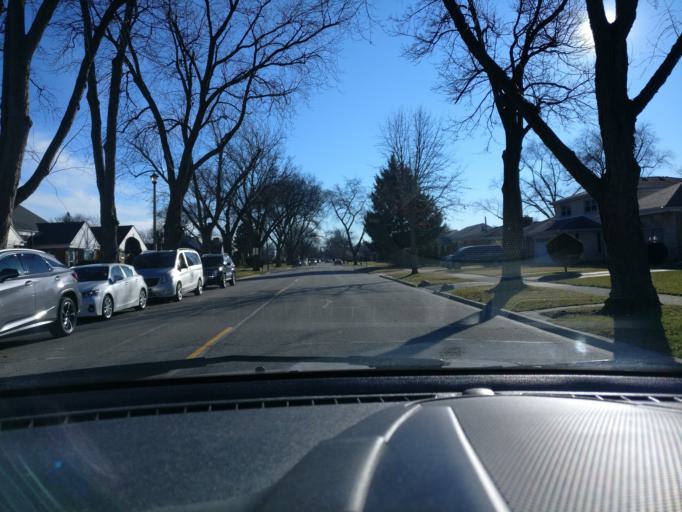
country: US
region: Illinois
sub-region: Cook County
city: Skokie
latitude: 42.0370
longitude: -87.7569
